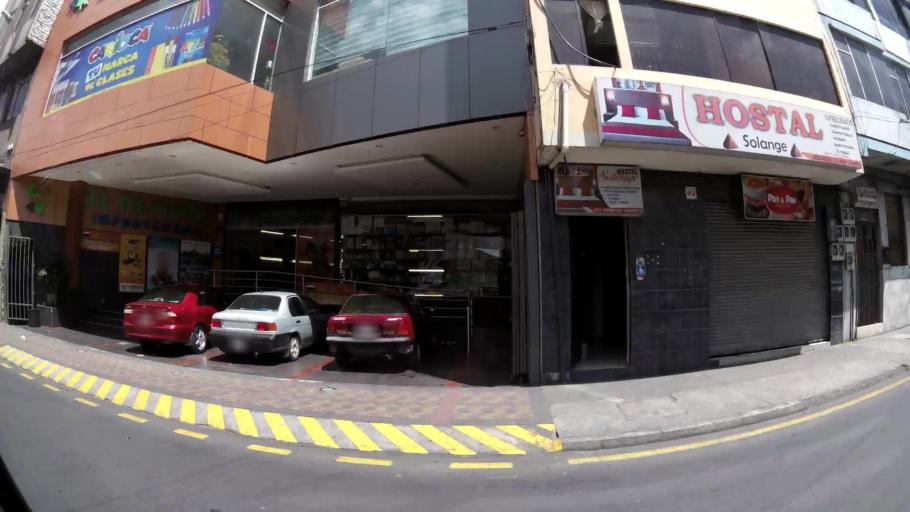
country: EC
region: Tungurahua
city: Ambato
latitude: -1.2396
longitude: -78.6238
